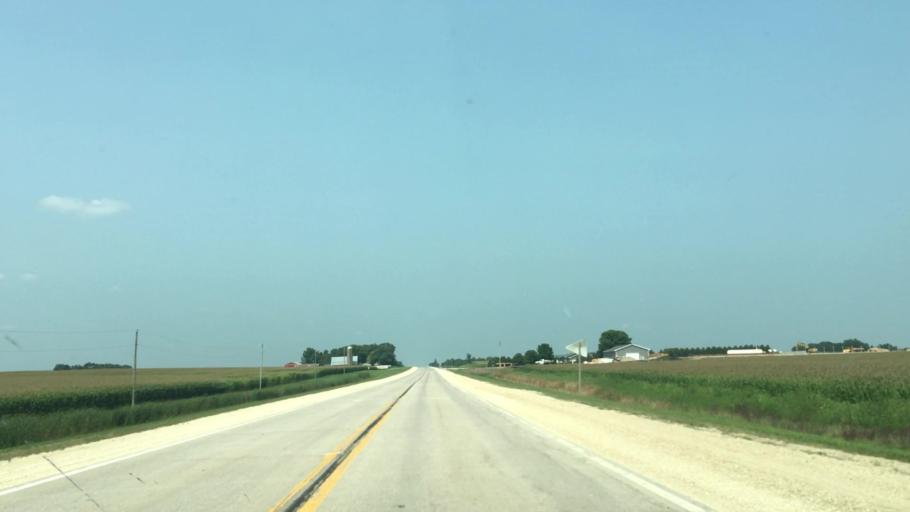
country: US
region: Iowa
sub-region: Fayette County
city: Fayette
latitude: 42.7637
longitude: -91.8045
